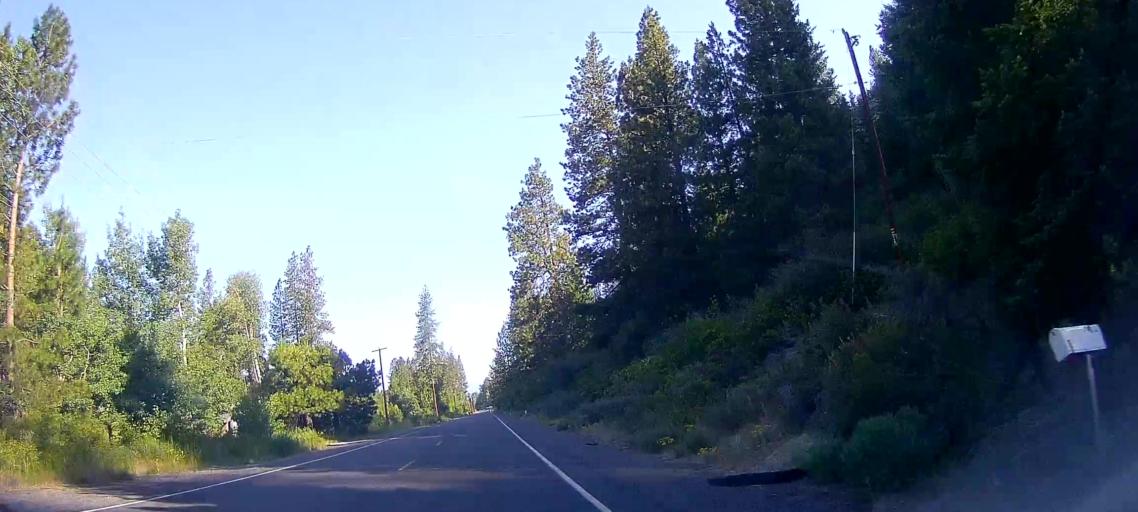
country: US
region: Oregon
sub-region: Klamath County
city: Klamath Falls
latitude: 42.6371
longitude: -121.9398
